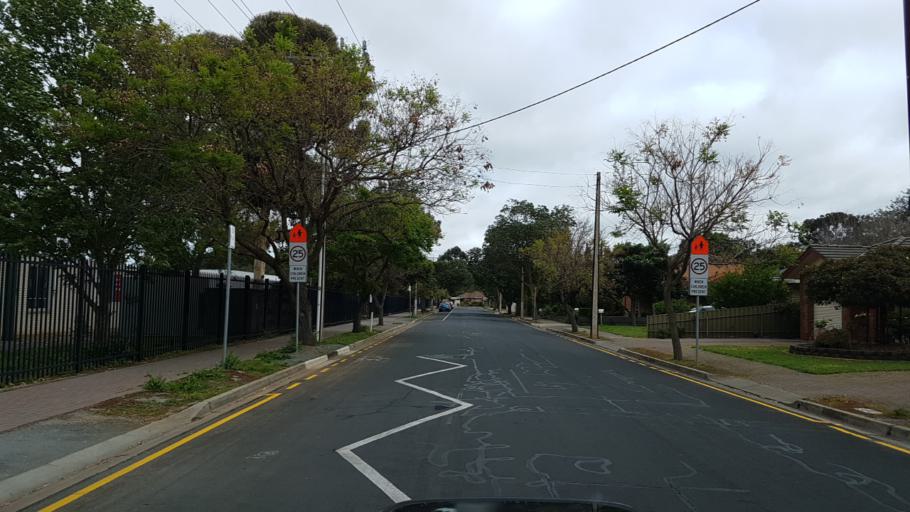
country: AU
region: South Australia
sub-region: Norwood Payneham St Peters
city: Marden
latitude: -34.8913
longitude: 138.6371
